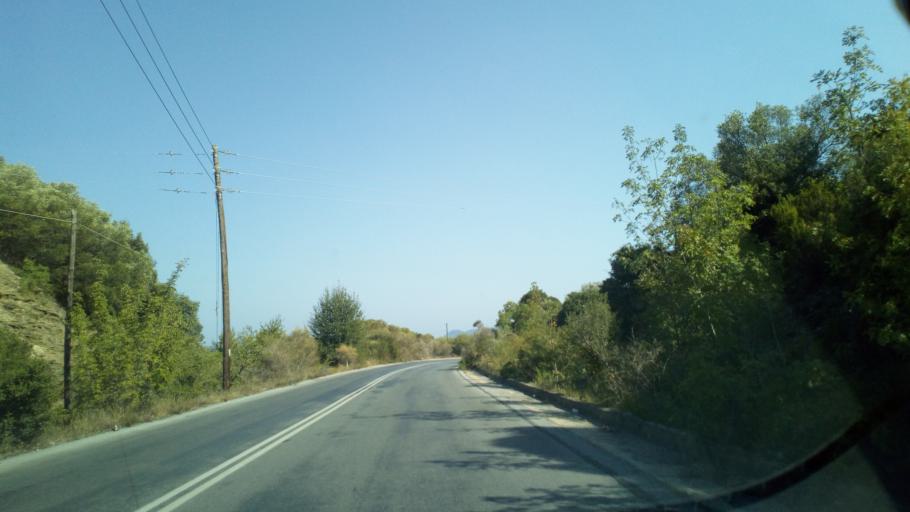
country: GR
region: Central Macedonia
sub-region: Nomos Thessalonikis
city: Stavros
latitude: 40.6159
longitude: 23.7760
